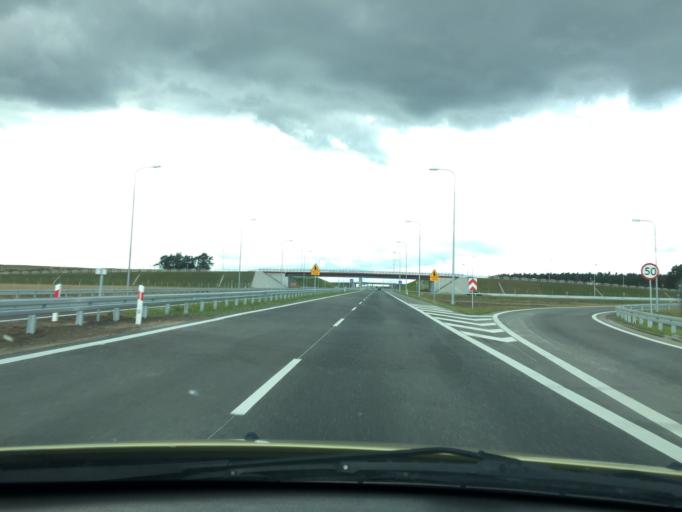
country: PL
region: Greater Poland Voivodeship
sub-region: Powiat jarocinski
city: Jarocin
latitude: 52.0336
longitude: 17.4691
